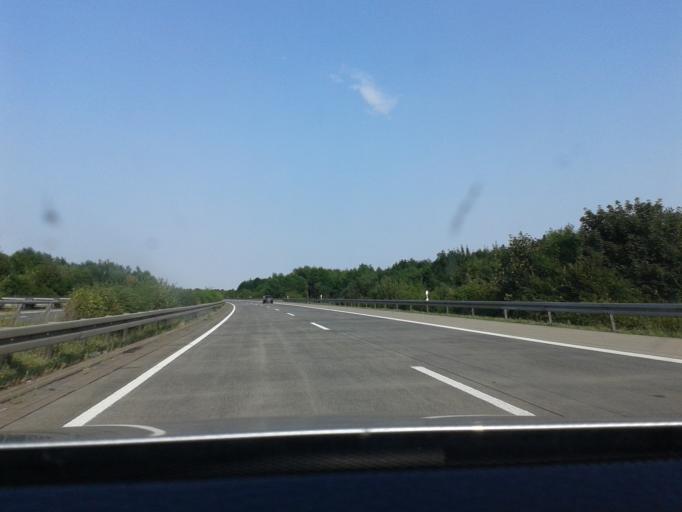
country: DE
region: Thuringia
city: Uthleben
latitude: 51.4583
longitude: 10.8185
